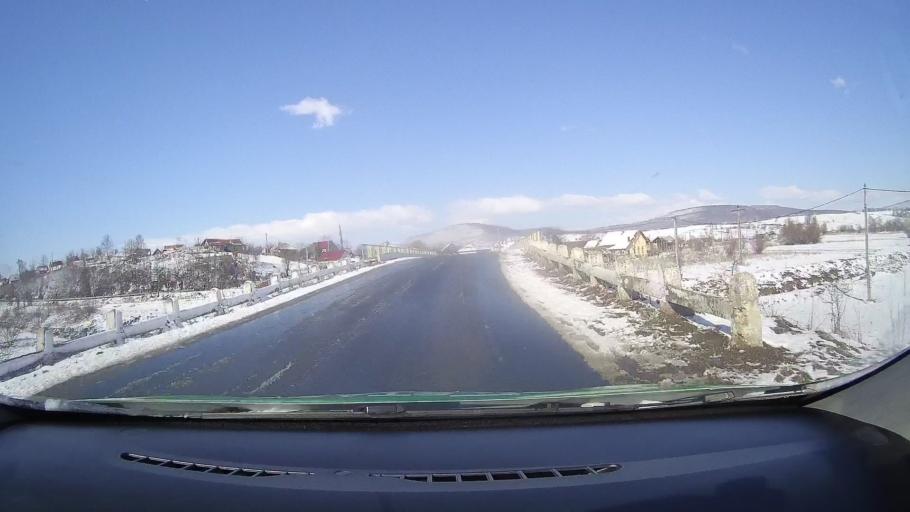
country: RO
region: Sibiu
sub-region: Comuna Rosia
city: Rosia
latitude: 45.8014
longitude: 24.3536
